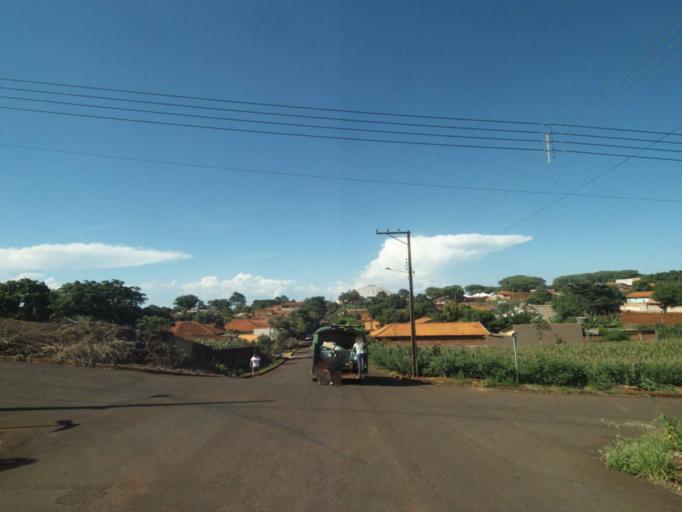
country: BR
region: Parana
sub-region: Sertanopolis
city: Sertanopolis
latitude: -23.0374
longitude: -50.8144
